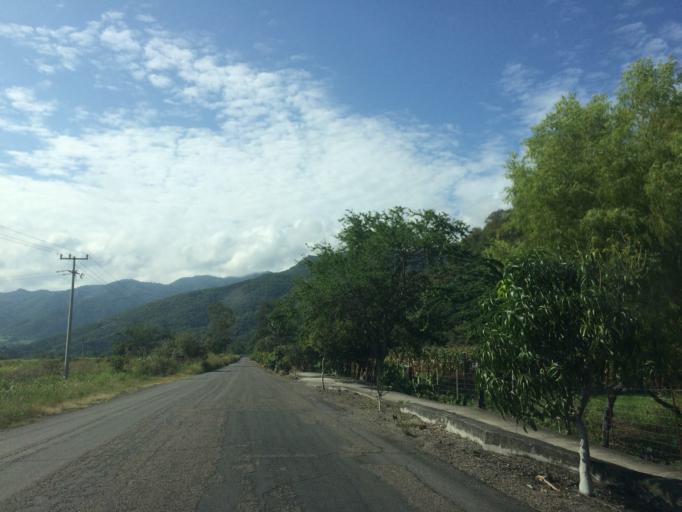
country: MX
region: Nayarit
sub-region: Ahuacatlan
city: Ahuacatlan
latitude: 21.0416
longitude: -104.4734
